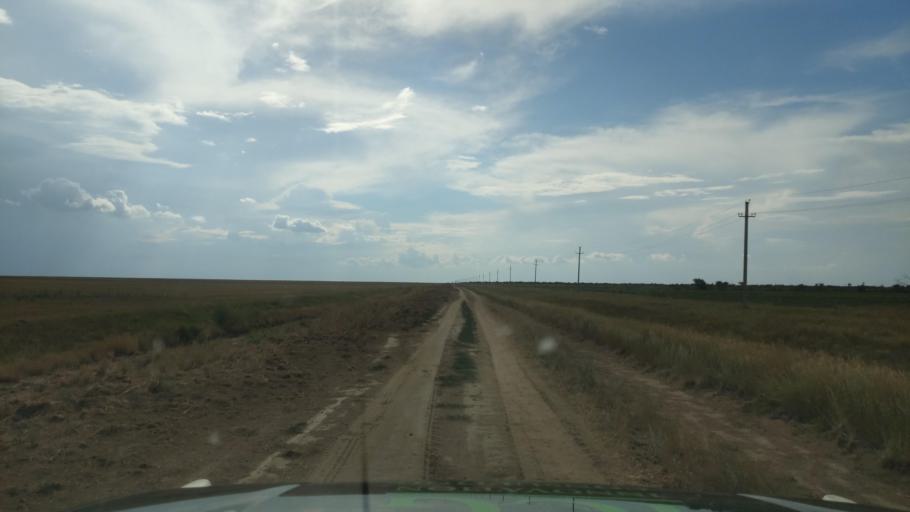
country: KZ
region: Pavlodar
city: Pavlodar
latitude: 52.5122
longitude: 77.5363
